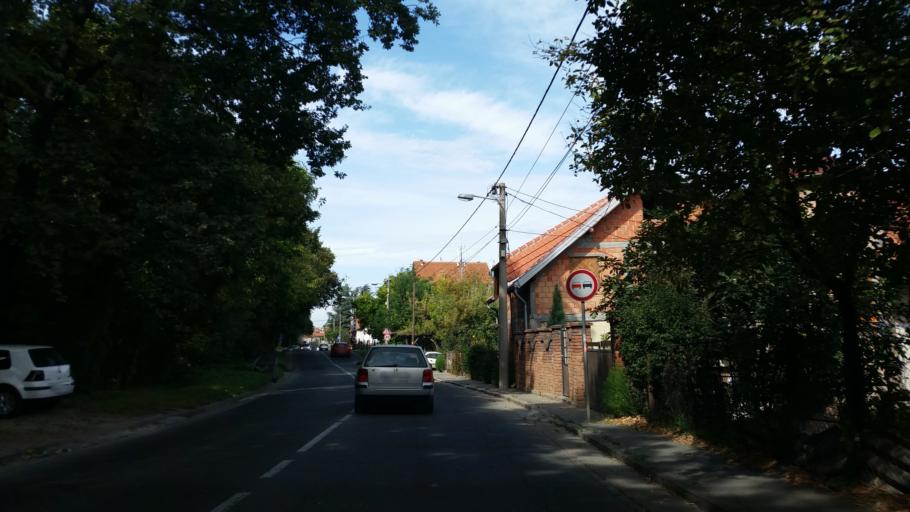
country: RS
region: Central Serbia
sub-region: Belgrade
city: Palilula
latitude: 44.8111
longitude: 20.5090
